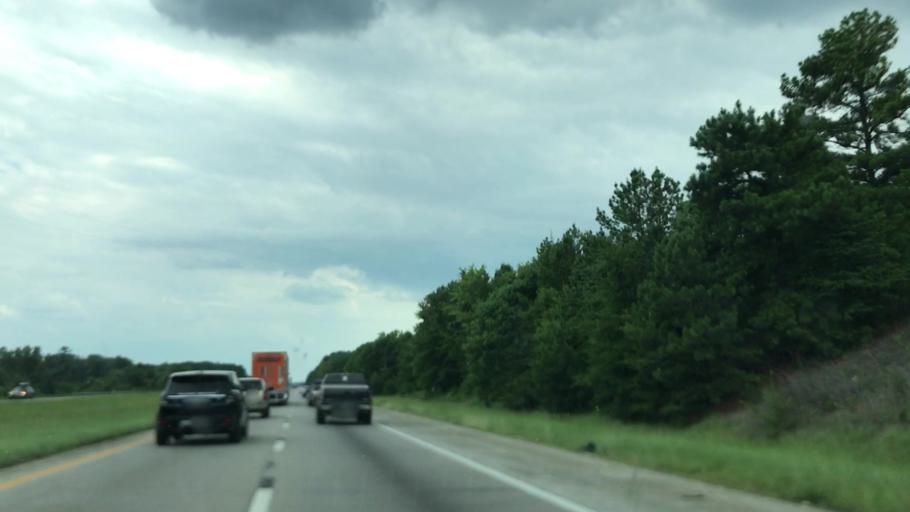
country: US
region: South Carolina
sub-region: Fairfield County
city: Winnsboro Mills
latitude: 34.3531
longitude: -80.9992
